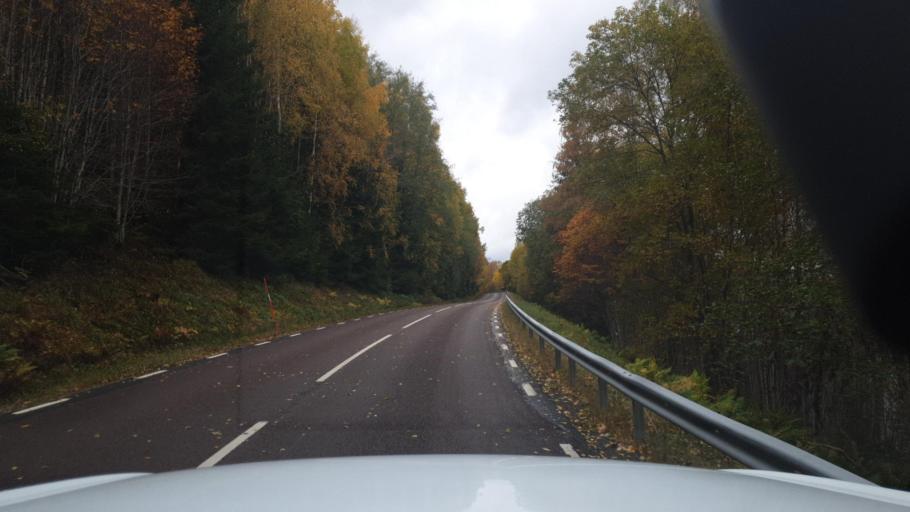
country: SE
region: Vaermland
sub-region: Sunne Kommun
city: Sunne
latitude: 59.8226
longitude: 12.9973
